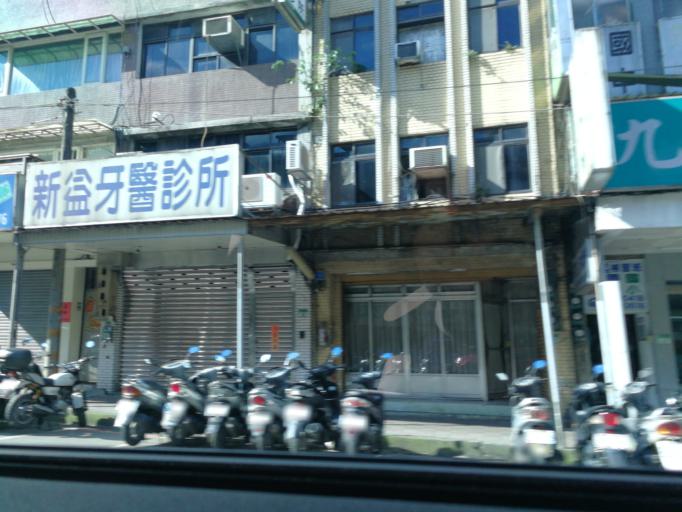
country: TW
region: Taipei
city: Taipei
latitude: 24.9564
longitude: 121.5384
